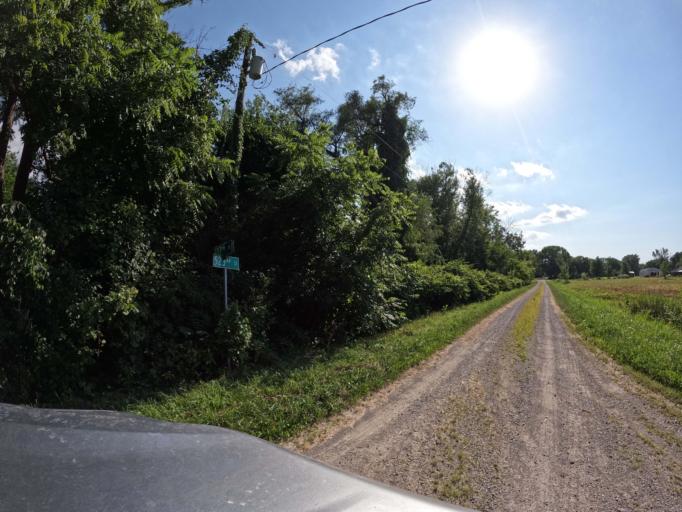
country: US
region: Iowa
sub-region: Appanoose County
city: Centerville
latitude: 40.7188
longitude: -93.0284
